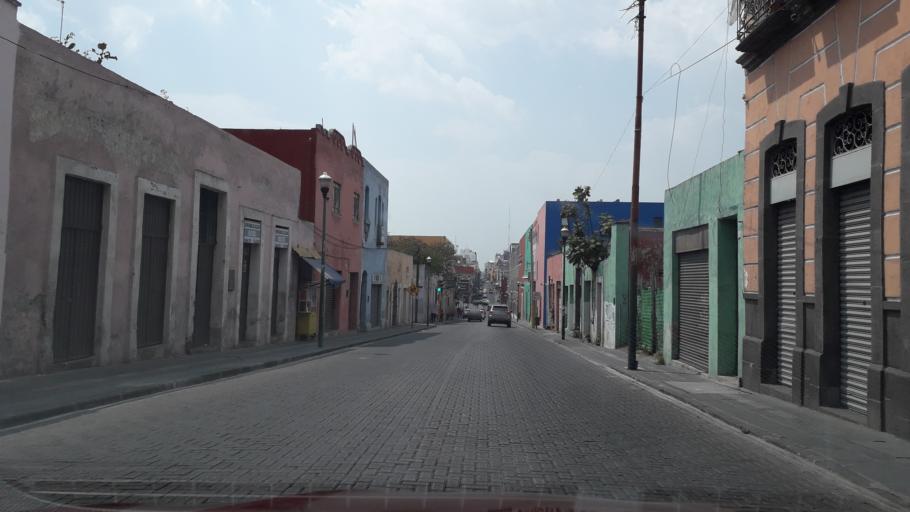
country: MX
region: Puebla
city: Puebla
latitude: 19.0412
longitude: -98.1906
